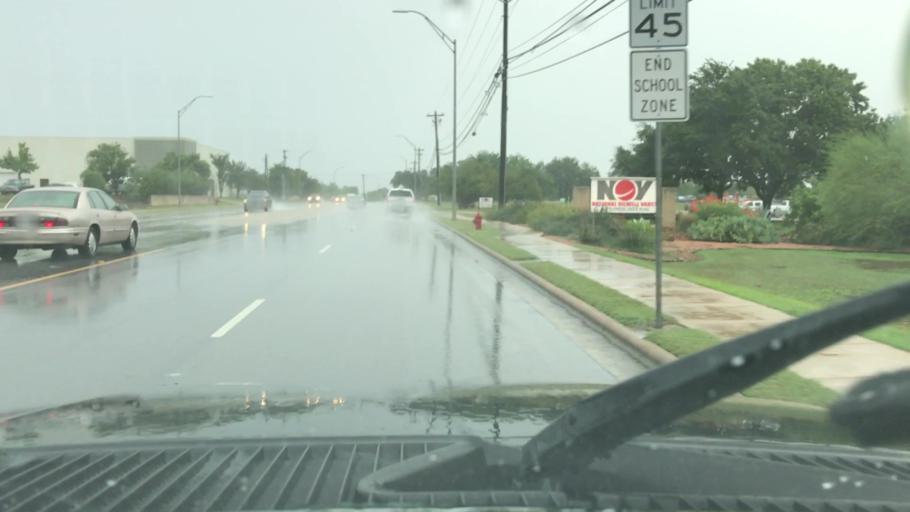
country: US
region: Texas
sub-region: Williamson County
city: Cedar Park
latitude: 30.4900
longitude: -97.8289
